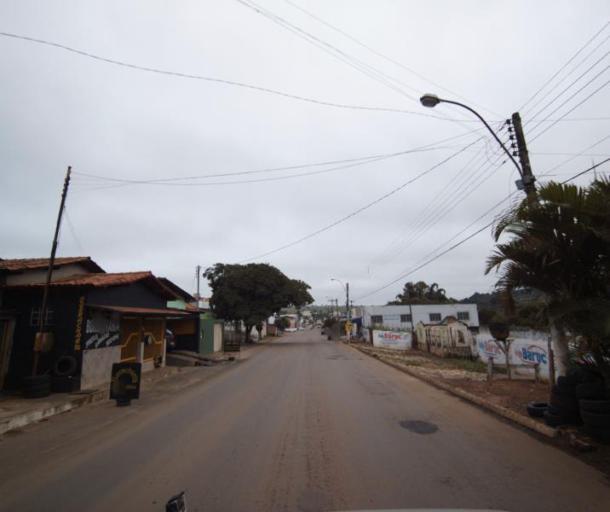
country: BR
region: Goias
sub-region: Pirenopolis
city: Pirenopolis
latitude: -15.9280
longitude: -48.8054
